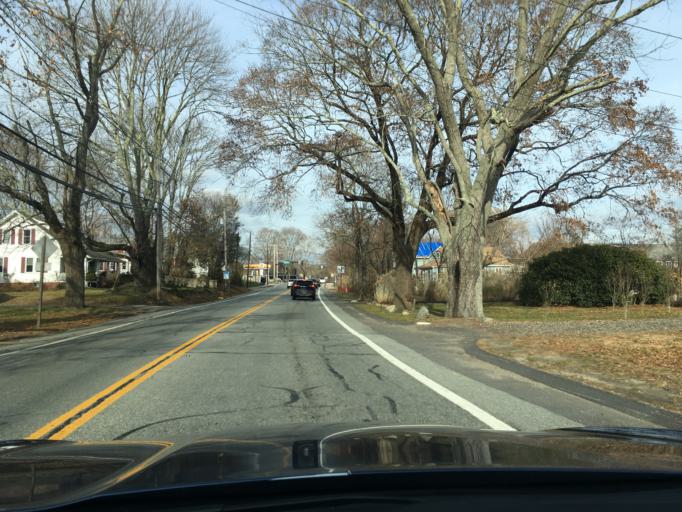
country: US
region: Rhode Island
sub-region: Washington County
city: North Kingstown
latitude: 41.5644
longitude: -71.4642
